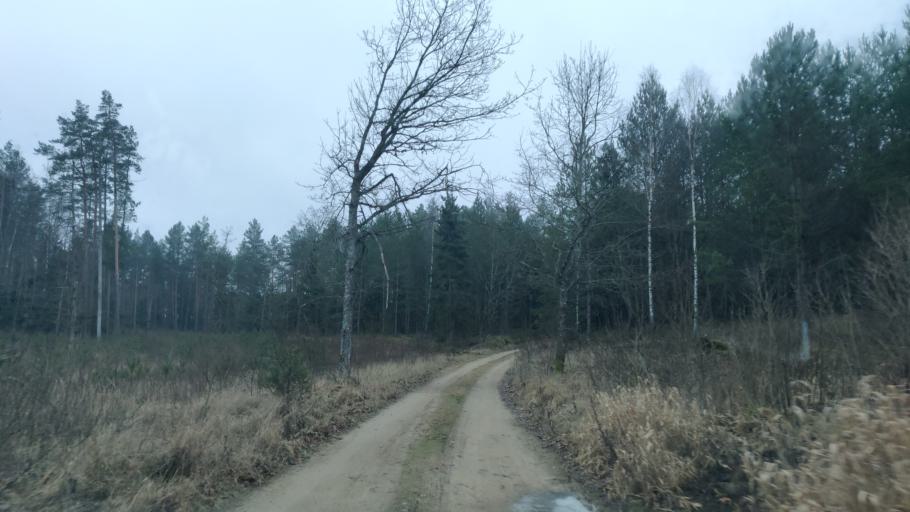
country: LT
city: Trakai
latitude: 54.5596
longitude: 24.9579
